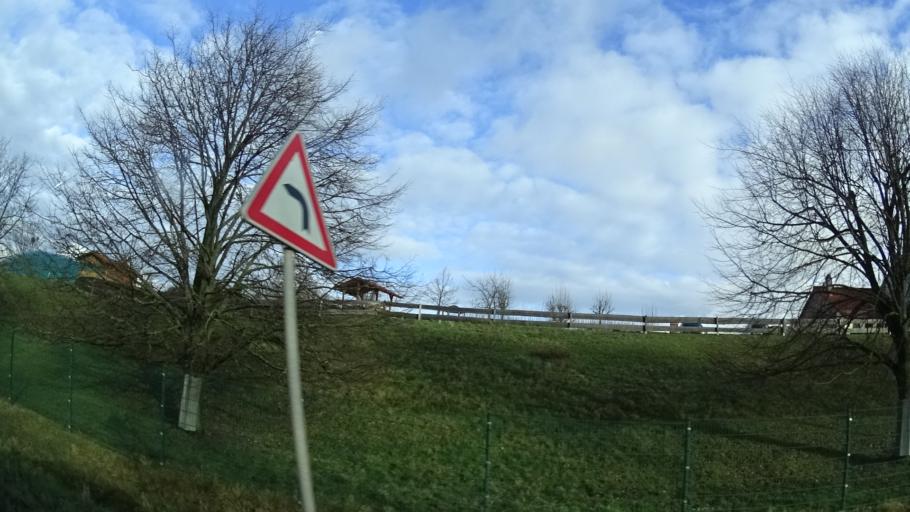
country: DE
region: Thuringia
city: Dermbach
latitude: 50.7149
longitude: 10.1453
